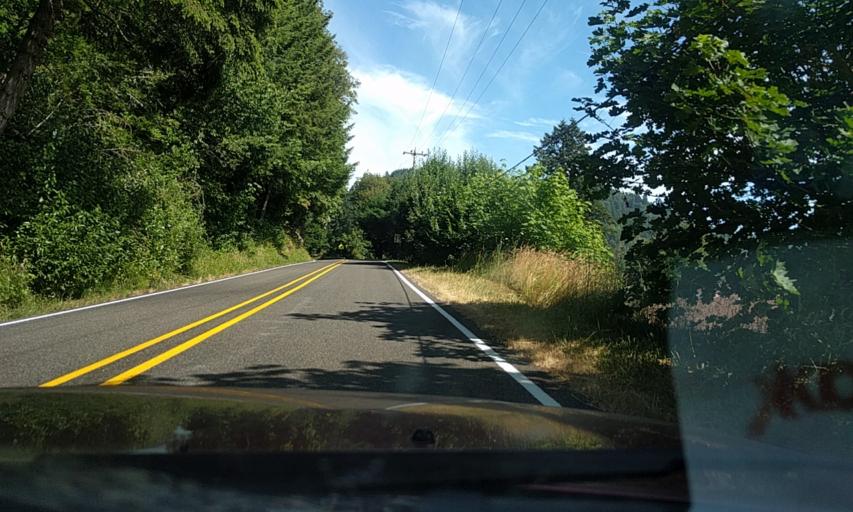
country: US
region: Oregon
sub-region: Lane County
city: Florence
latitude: 44.0374
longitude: -123.8602
